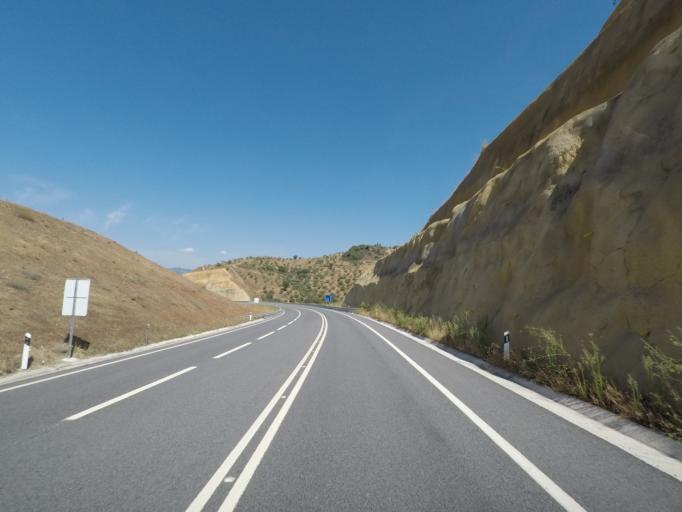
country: PT
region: Braganca
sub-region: Alfandega da Fe
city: Alfandega da Fe
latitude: 41.2935
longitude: -6.8959
